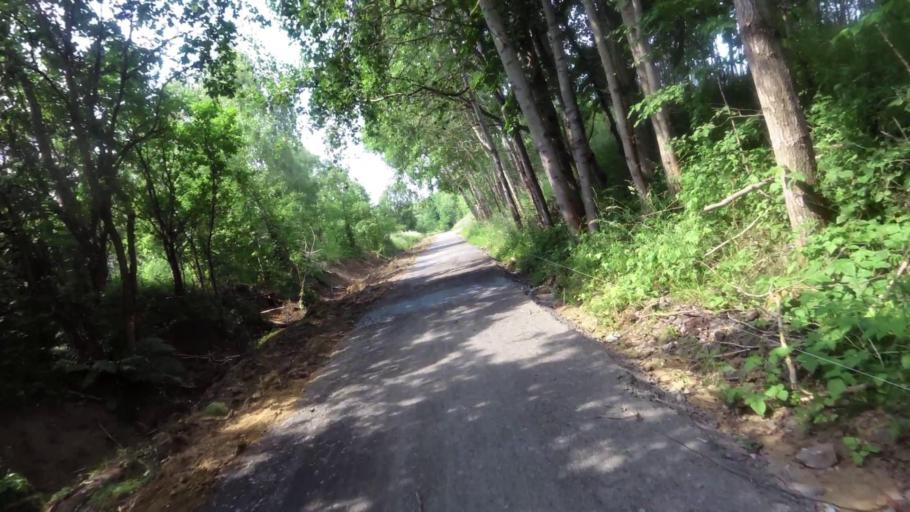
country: PL
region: West Pomeranian Voivodeship
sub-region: Powiat pyrzycki
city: Bielice
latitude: 53.2073
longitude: 14.6142
